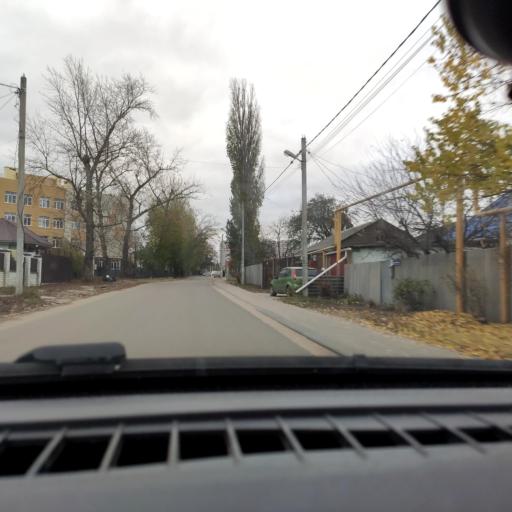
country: RU
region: Voronezj
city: Podgornoye
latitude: 51.7318
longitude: 39.1585
